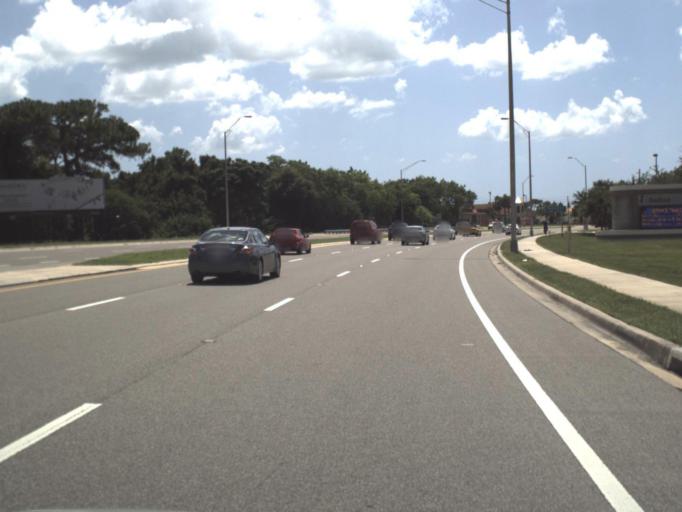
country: US
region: Florida
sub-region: Pinellas County
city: Ridgecrest
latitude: 27.8834
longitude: -82.8126
